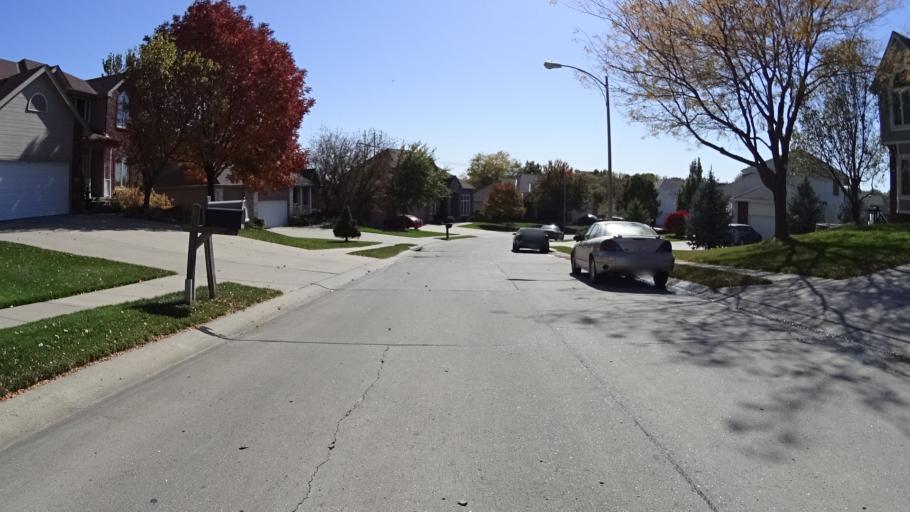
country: US
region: Nebraska
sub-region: Sarpy County
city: La Vista
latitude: 41.1707
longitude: -96.0246
